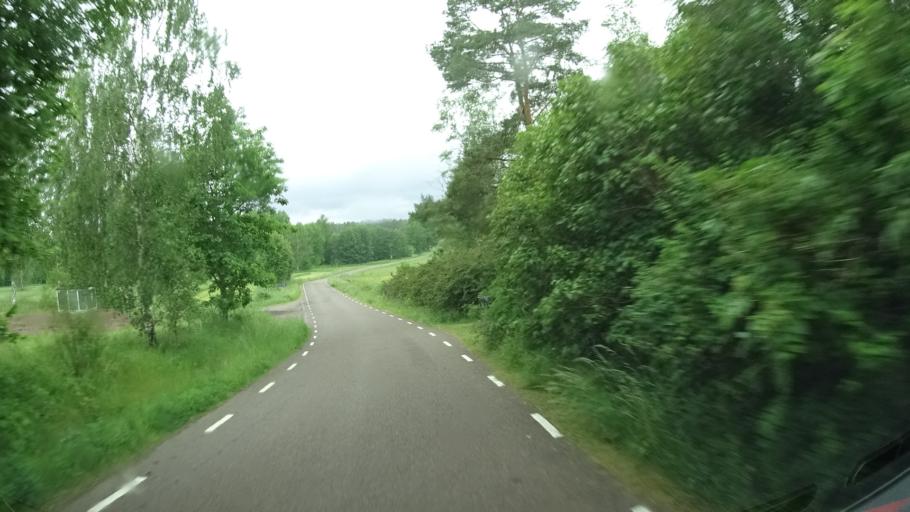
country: SE
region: Kalmar
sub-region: Vimmerby Kommun
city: Sodra Vi
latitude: 57.7035
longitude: 15.7472
